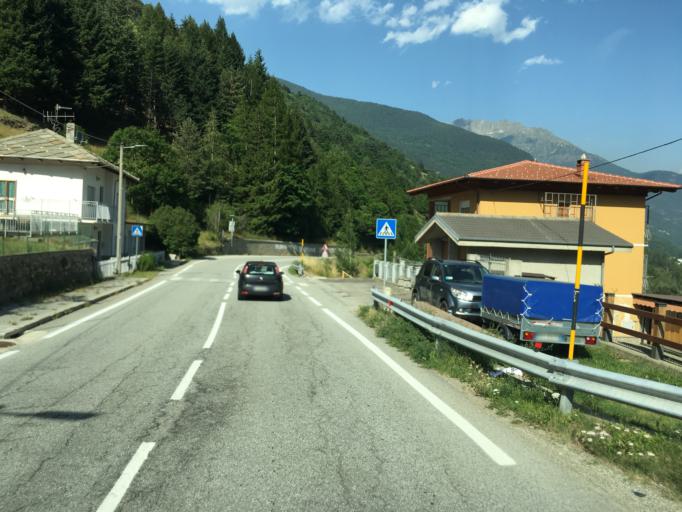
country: IT
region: Piedmont
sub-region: Provincia di Torino
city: Fenestrelle
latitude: 45.0264
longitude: 7.0680
